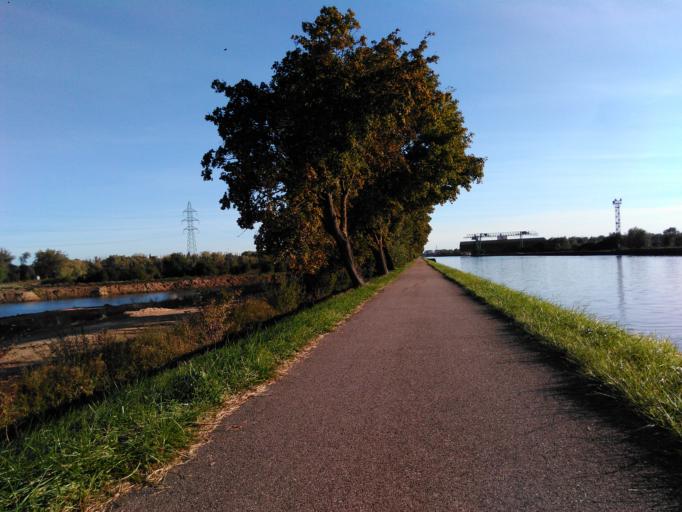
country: FR
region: Lorraine
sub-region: Departement de la Moselle
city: Bousse
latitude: 49.2758
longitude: 6.1821
